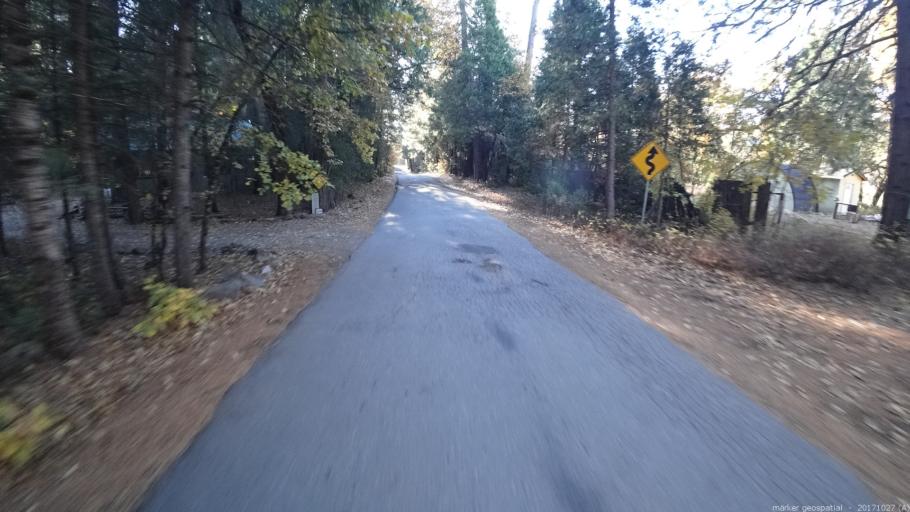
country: US
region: California
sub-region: Shasta County
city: Burney
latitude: 41.0131
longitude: -121.9036
